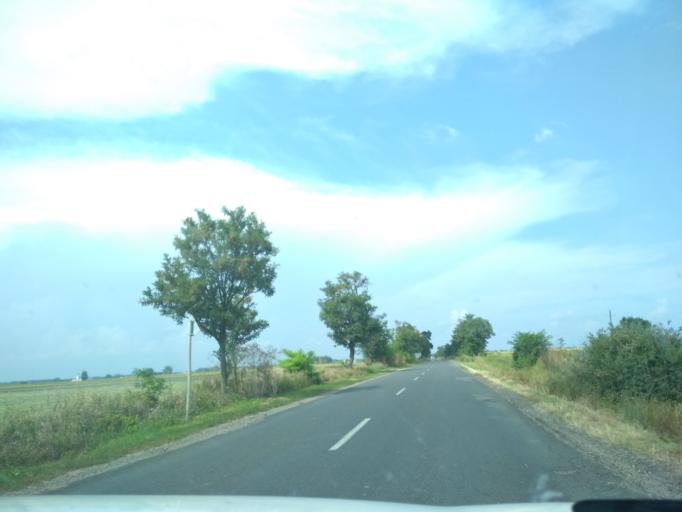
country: HU
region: Jasz-Nagykun-Szolnok
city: Tiszaszolos
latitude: 47.5349
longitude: 20.7145
